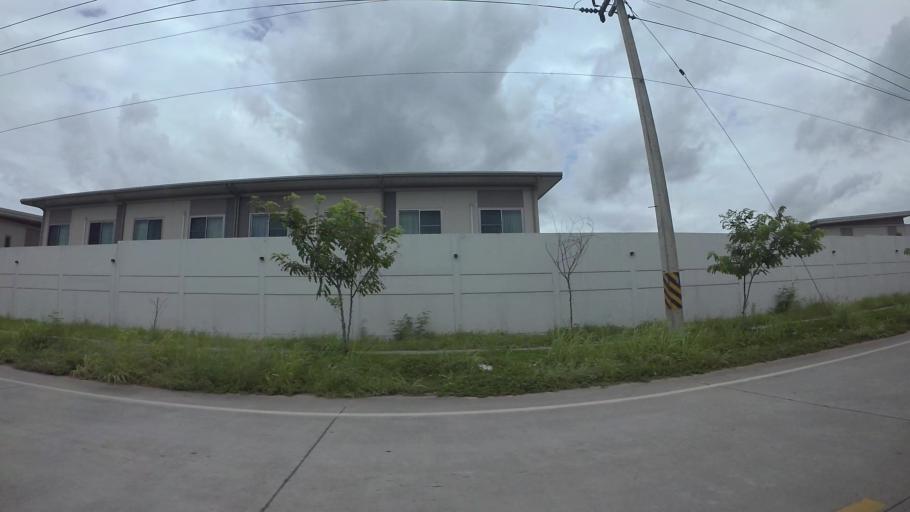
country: TH
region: Chon Buri
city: Si Racha
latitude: 13.1625
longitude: 100.9859
